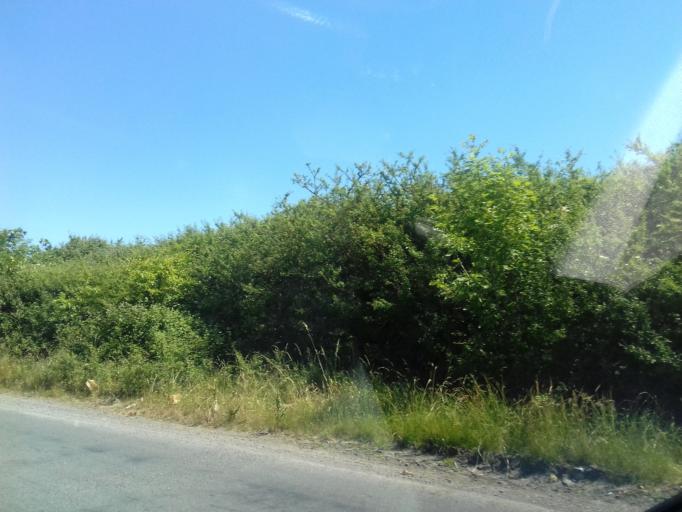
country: IE
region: Leinster
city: Ballymun
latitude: 53.4405
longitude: -6.2932
